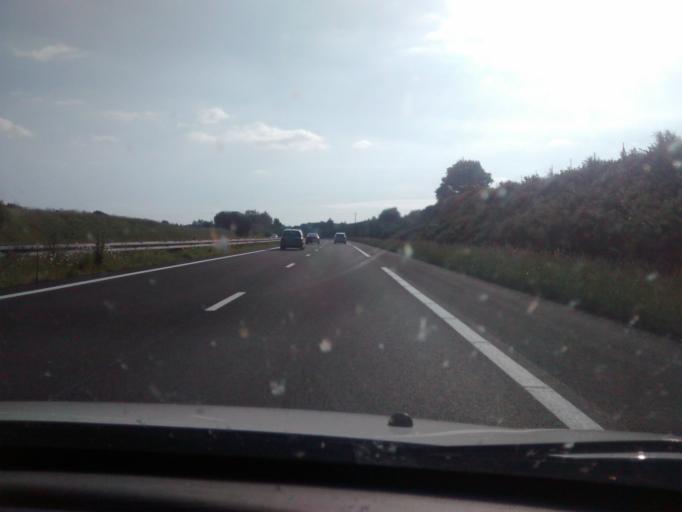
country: FR
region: Pays de la Loire
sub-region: Departement de la Mayenne
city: Change
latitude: 48.1116
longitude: -0.8202
